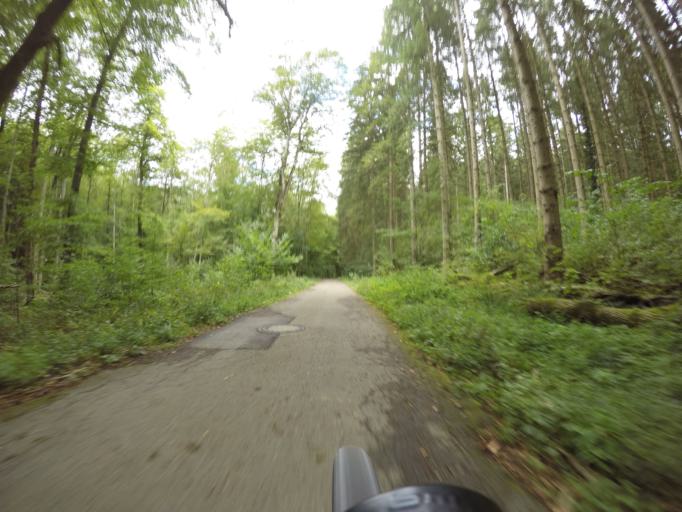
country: DE
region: Baden-Wuerttemberg
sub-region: Tuebingen Region
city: Reutlingen
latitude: 48.4653
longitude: 9.1733
